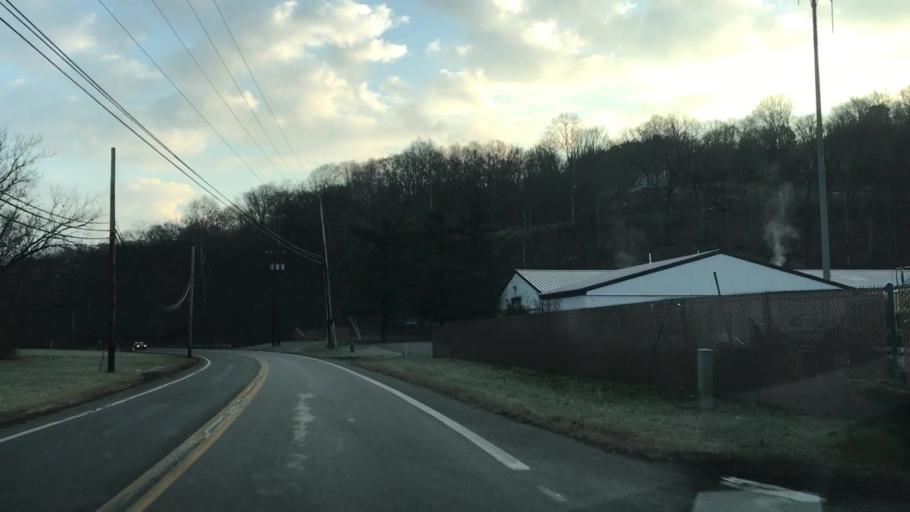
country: US
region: Pennsylvania
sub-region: Allegheny County
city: Carnot-Moon
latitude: 40.5300
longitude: -80.2333
